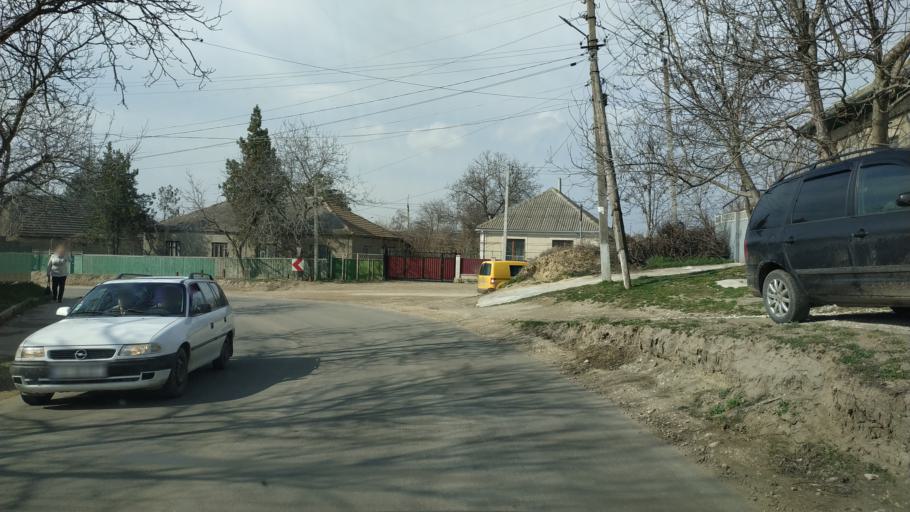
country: MD
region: Gagauzia
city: Vulcanesti
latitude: 45.6776
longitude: 28.4134
